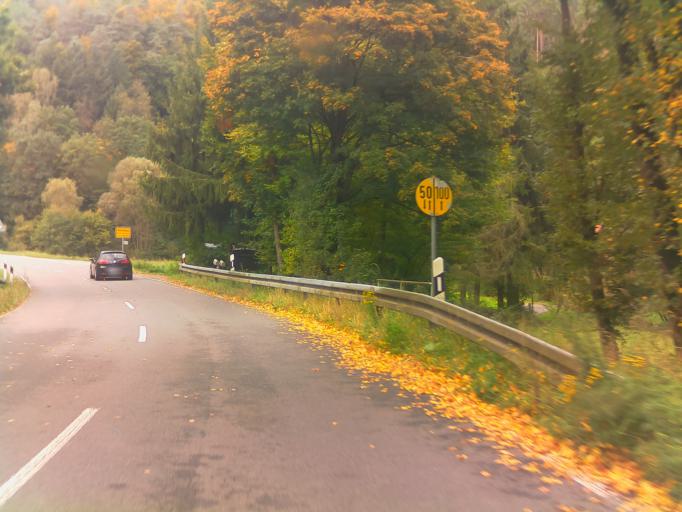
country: DE
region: Bavaria
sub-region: Regierungsbezirk Unterfranken
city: Kirchzell
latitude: 49.6267
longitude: 9.1394
